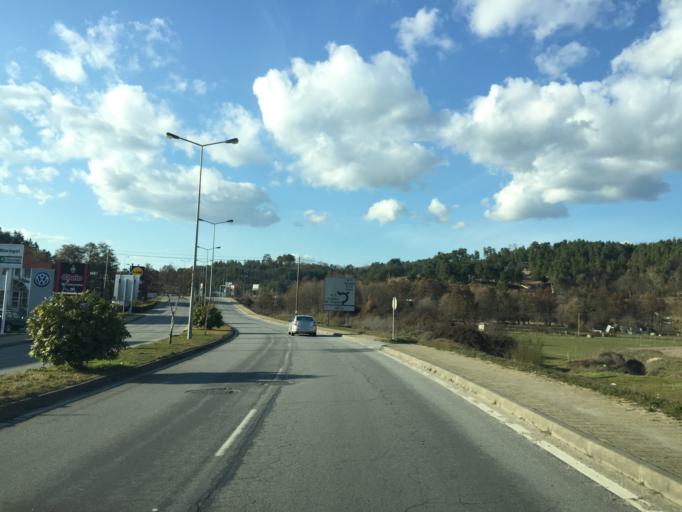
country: PT
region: Guarda
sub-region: Seia
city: Seia
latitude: 40.4297
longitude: -7.7158
